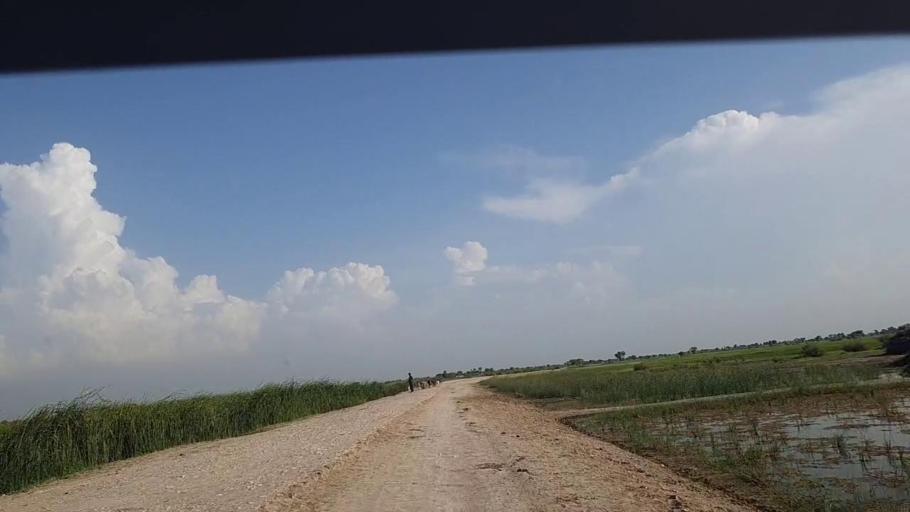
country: PK
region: Sindh
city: Khanpur
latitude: 27.8567
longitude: 69.3766
